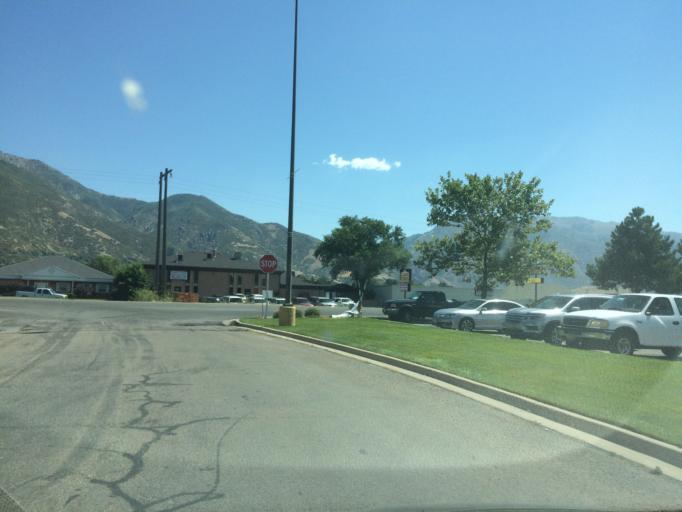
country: US
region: Utah
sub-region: Weber County
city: Uintah
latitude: 41.1577
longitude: -111.9404
